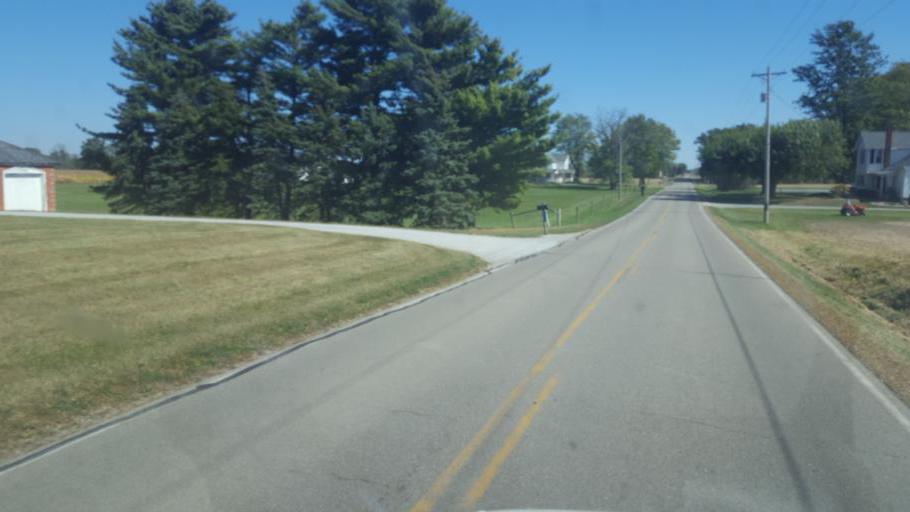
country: US
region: Ohio
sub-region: Huron County
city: Willard
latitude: 40.9819
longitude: -82.7880
